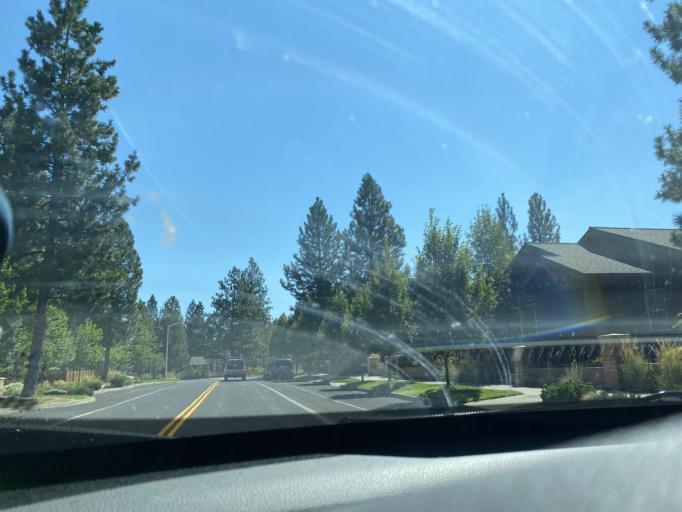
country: US
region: Oregon
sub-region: Deschutes County
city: Bend
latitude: 44.0589
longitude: -121.3533
